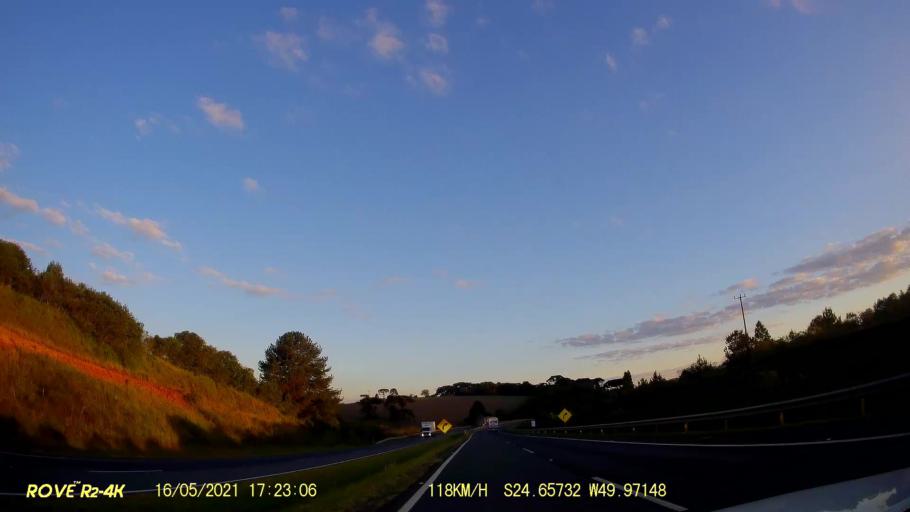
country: BR
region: Parana
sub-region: Pirai Do Sul
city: Pirai do Sul
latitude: -24.6577
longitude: -49.9713
